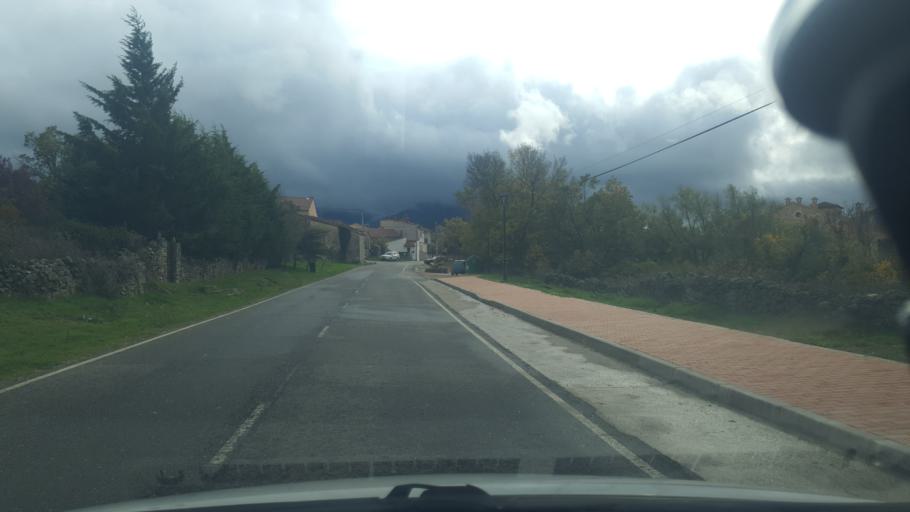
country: ES
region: Castille and Leon
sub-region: Provincia de Segovia
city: Gallegos
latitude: 41.0772
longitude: -3.7863
